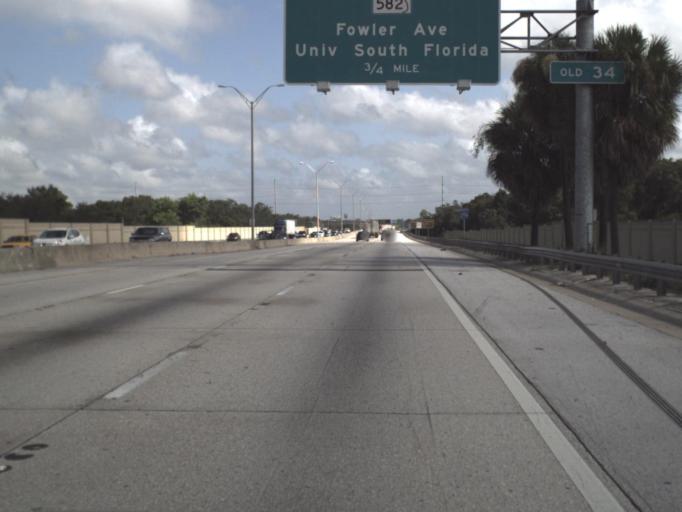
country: US
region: Florida
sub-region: Hillsborough County
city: University
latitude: 28.0402
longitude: -82.4548
